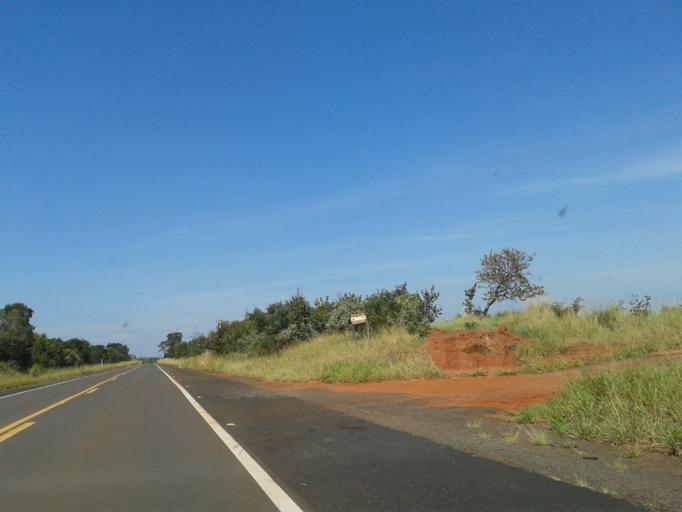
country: BR
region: Minas Gerais
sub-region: Campina Verde
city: Campina Verde
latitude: -19.4818
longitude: -49.5665
